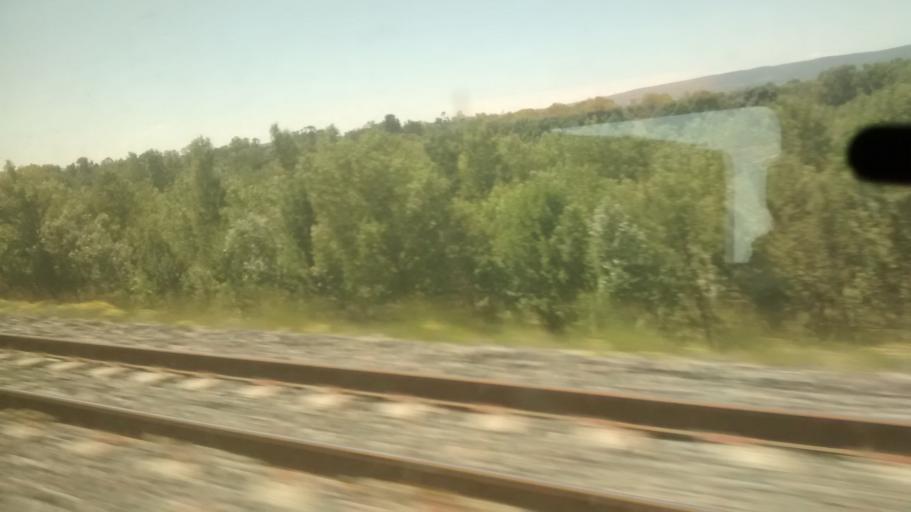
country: FR
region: Rhone-Alpes
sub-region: Departement de la Drome
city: La Garde-Adhemar
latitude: 44.3816
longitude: 4.7344
